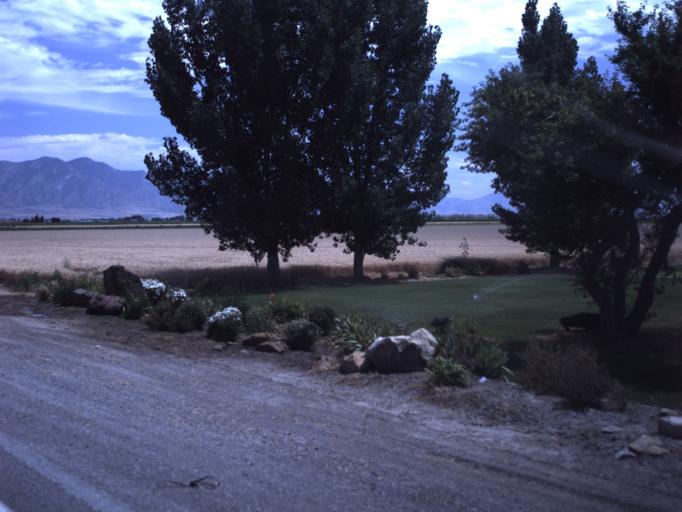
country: US
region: Utah
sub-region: Box Elder County
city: Tremonton
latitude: 41.7094
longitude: -112.2727
